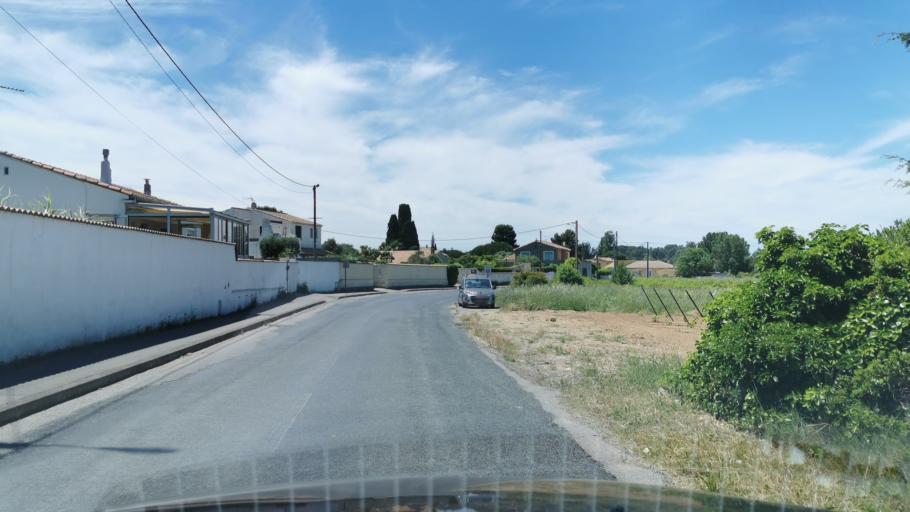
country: FR
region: Languedoc-Roussillon
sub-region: Departement de l'Aude
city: Nevian
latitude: 43.2140
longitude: 2.9107
